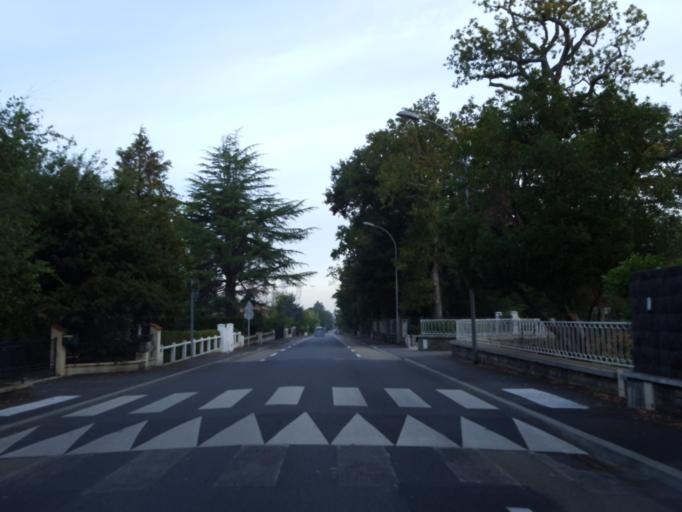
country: FR
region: Pays de la Loire
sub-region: Departement de la Loire-Atlantique
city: Basse-Goulaine
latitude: 47.1951
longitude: -1.4638
